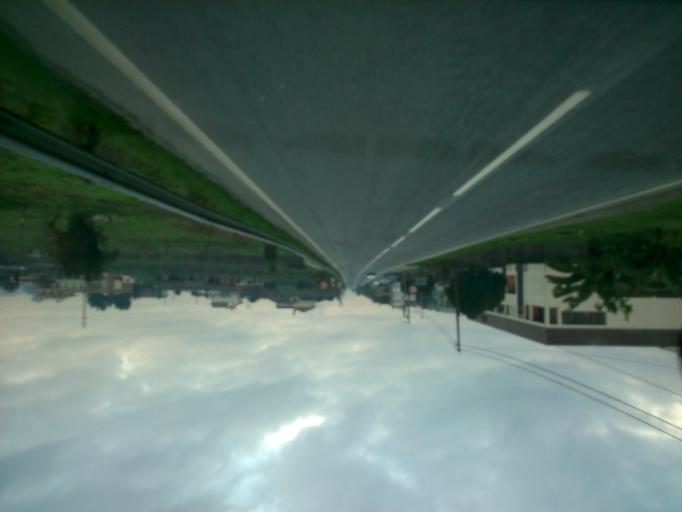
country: PT
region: Braga
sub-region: Barcelos
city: Barcelos
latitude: 41.5097
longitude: -8.5819
